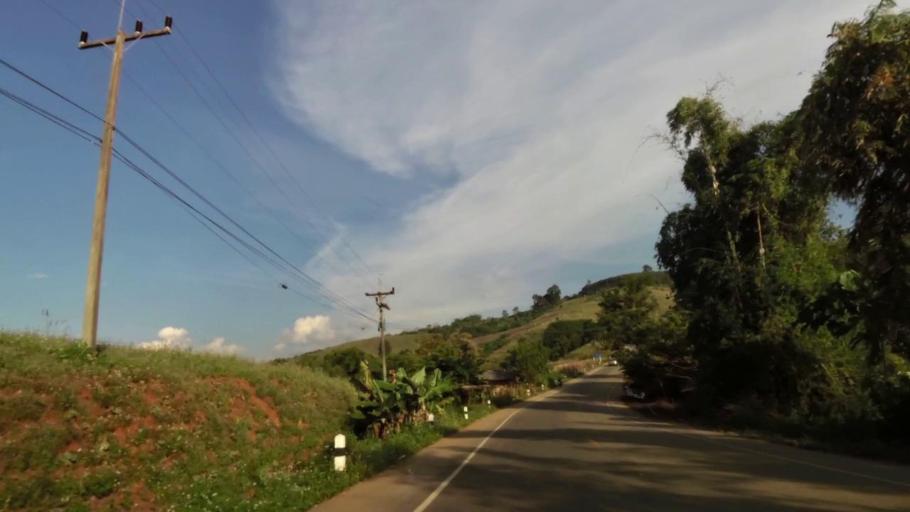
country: TH
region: Chiang Rai
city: Khun Tan
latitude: 19.8668
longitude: 100.4139
